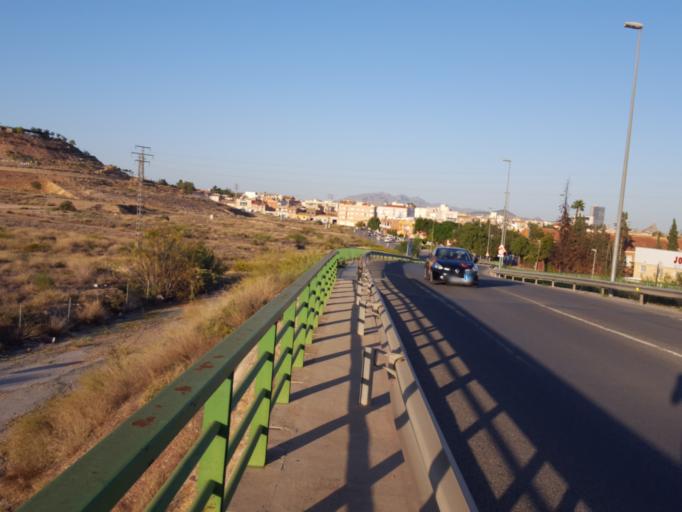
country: ES
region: Murcia
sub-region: Murcia
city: Murcia
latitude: 38.0045
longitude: -1.1653
